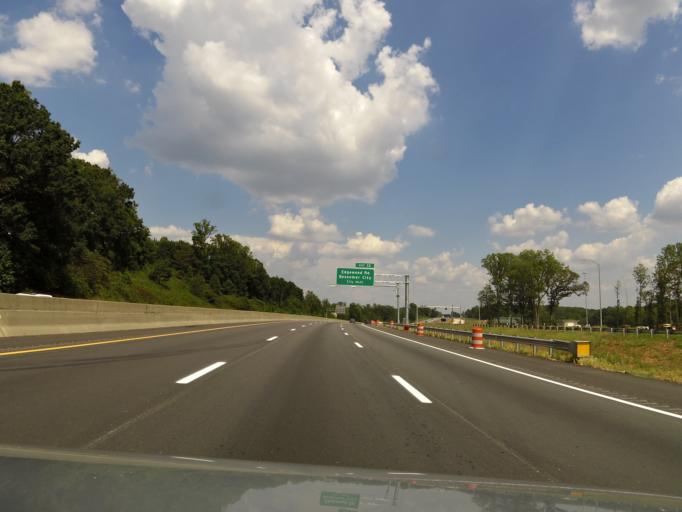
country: US
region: North Carolina
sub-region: Gaston County
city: Bessemer City
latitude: 35.2601
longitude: -81.2847
